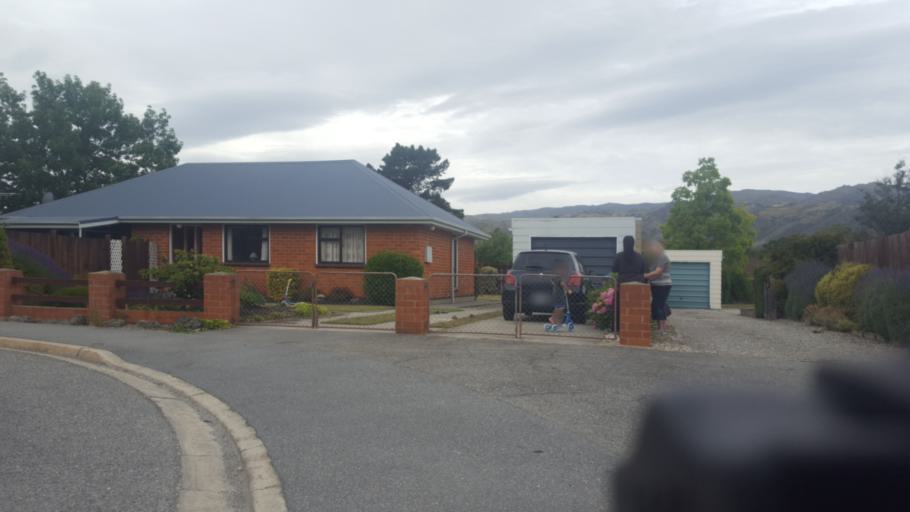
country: NZ
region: Otago
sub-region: Queenstown-Lakes District
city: Wanaka
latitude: -45.0411
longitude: 169.1903
